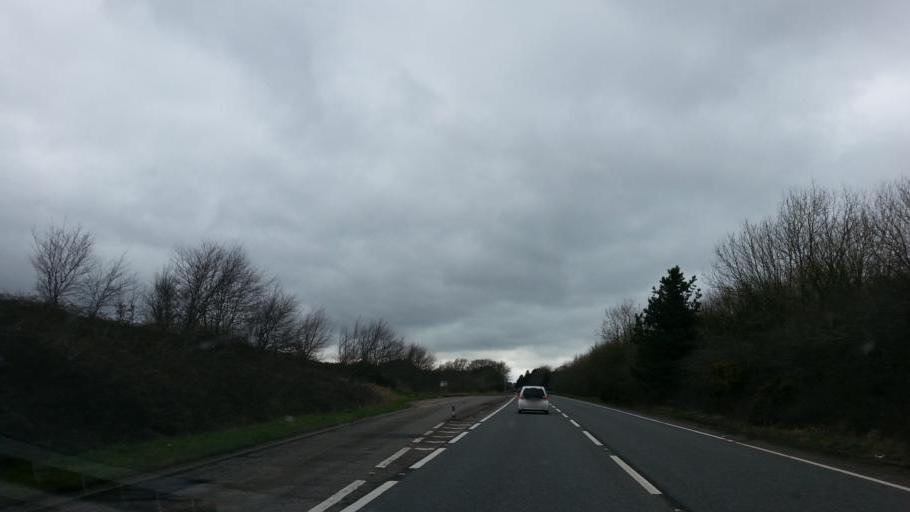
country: GB
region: England
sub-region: Devon
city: Tiverton
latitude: 50.9621
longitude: -3.6197
